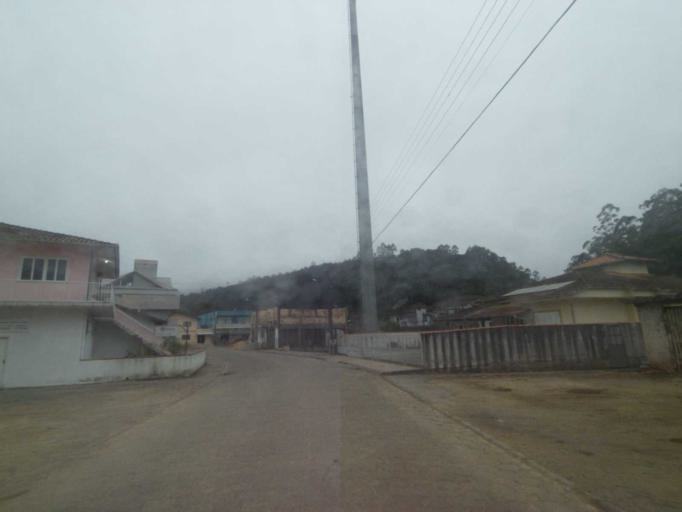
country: BR
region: Santa Catarina
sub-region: Anitapolis
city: Anitapolis
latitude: -27.9055
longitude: -49.1291
